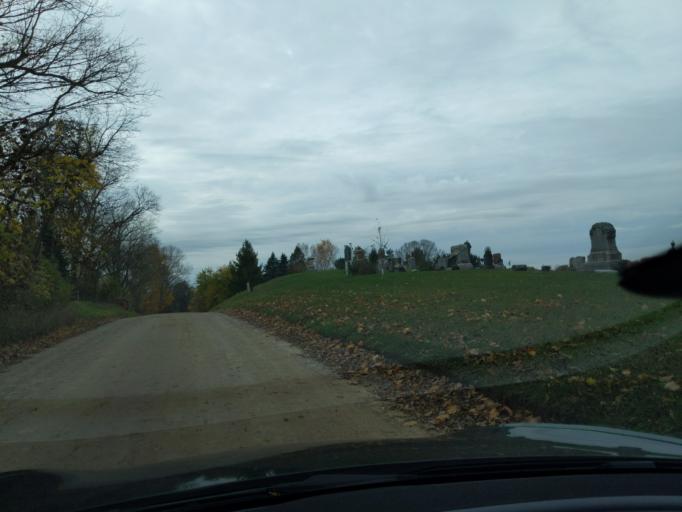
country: US
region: Michigan
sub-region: Eaton County
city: Eaton Rapids
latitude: 42.5532
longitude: -84.6037
